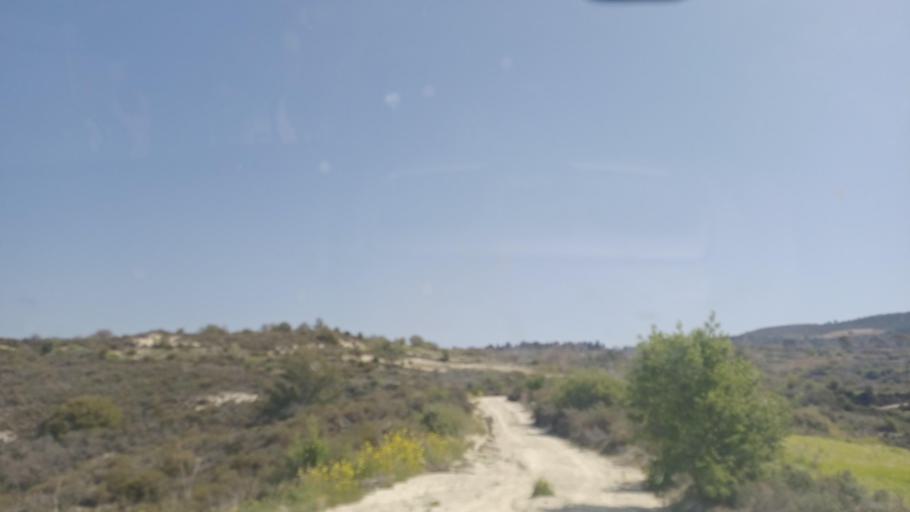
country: CY
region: Limassol
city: Pachna
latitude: 34.8607
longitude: 32.7426
